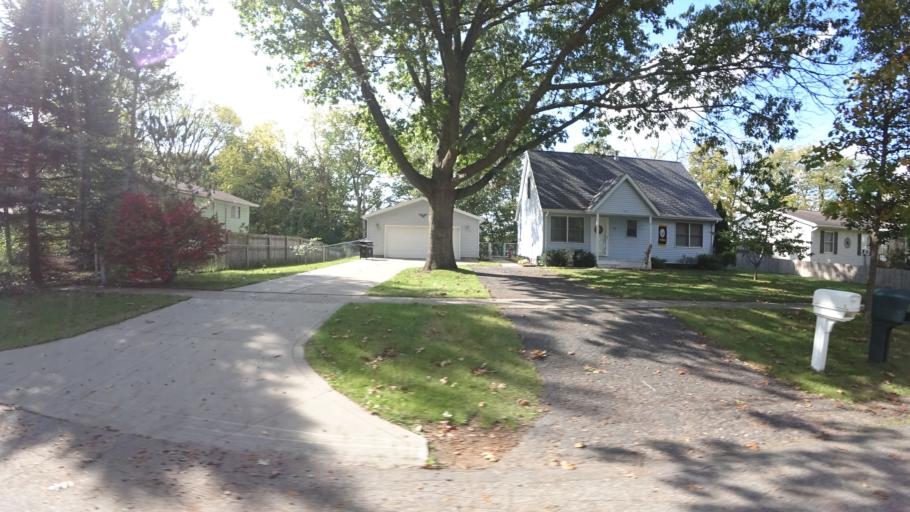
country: US
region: Michigan
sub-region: Saint Joseph County
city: Three Rivers
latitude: 41.9529
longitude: -85.6147
